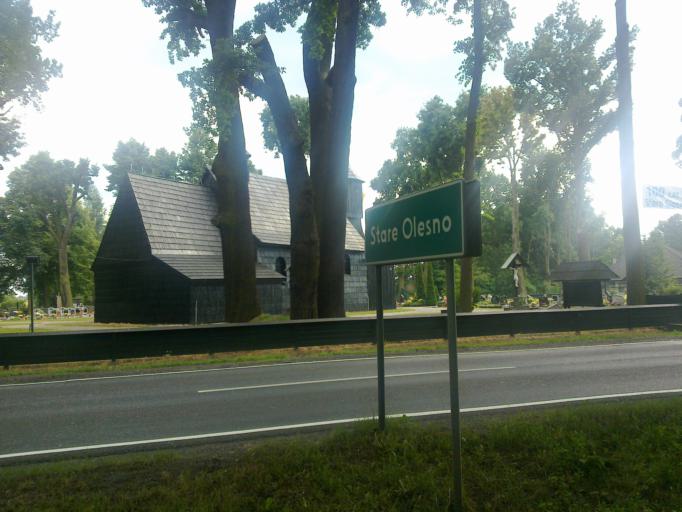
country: PL
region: Opole Voivodeship
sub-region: Powiat oleski
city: Olesno
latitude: 50.9097
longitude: 18.3588
